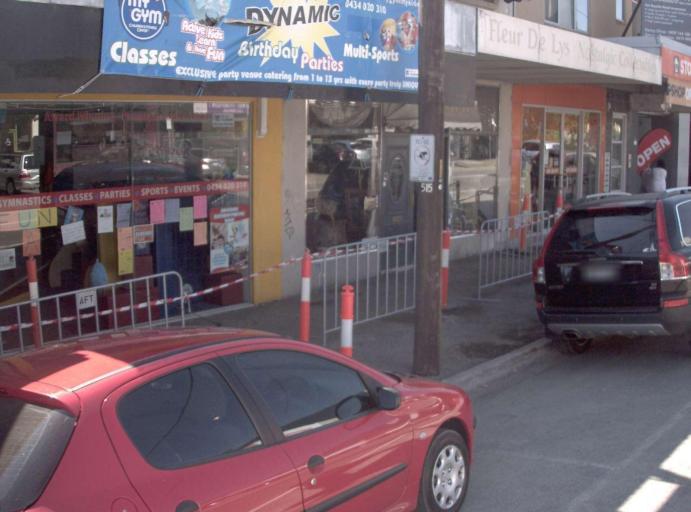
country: AU
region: Victoria
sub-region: Bayside
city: Hampton
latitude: -37.9320
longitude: 145.0035
